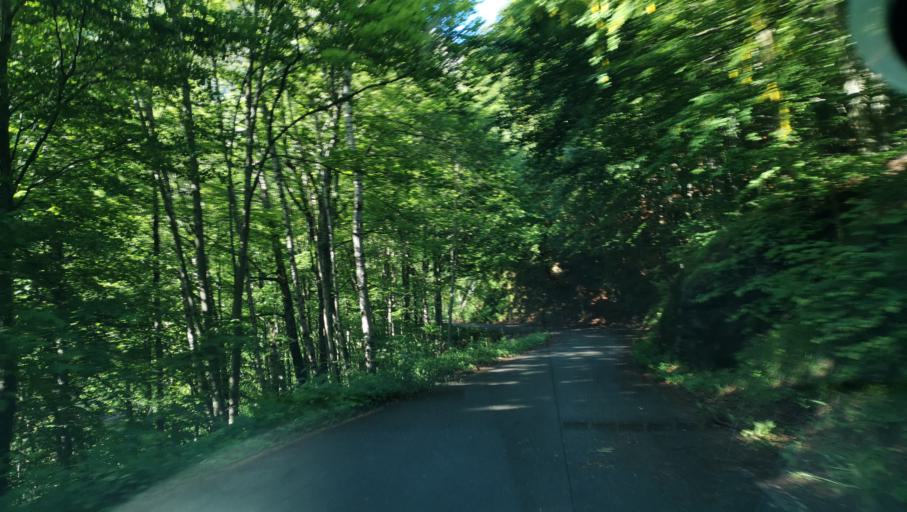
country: IT
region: Piedmont
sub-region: Provincia di Torino
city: Usseglio
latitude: 45.2177
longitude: 7.1857
